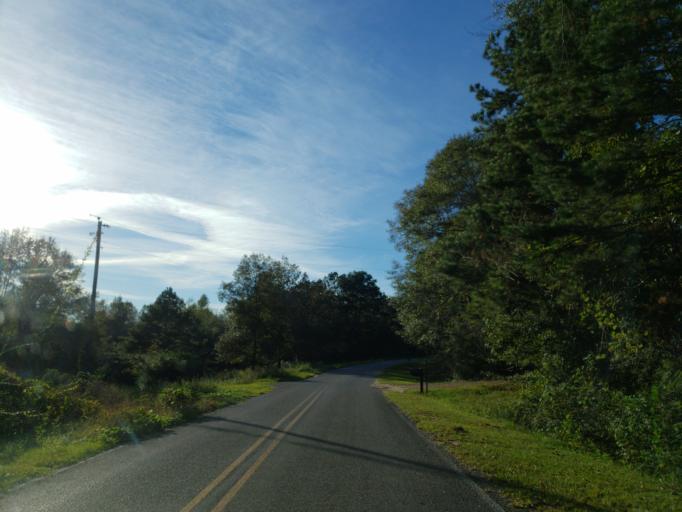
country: US
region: Mississippi
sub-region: Perry County
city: Richton
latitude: 31.3494
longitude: -88.8134
